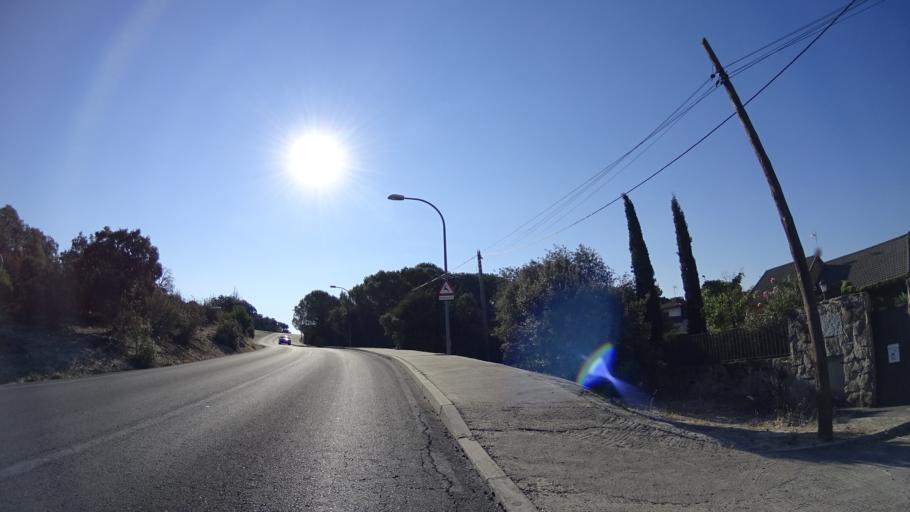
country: ES
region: Madrid
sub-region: Provincia de Madrid
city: Torrelodones
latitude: 40.5818
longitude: -3.9092
